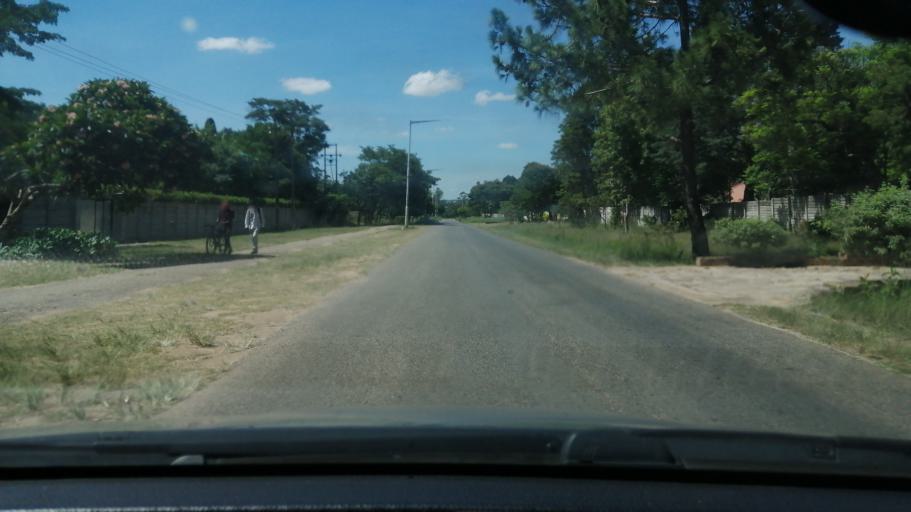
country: ZW
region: Harare
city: Epworth
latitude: -17.8274
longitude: 31.1253
